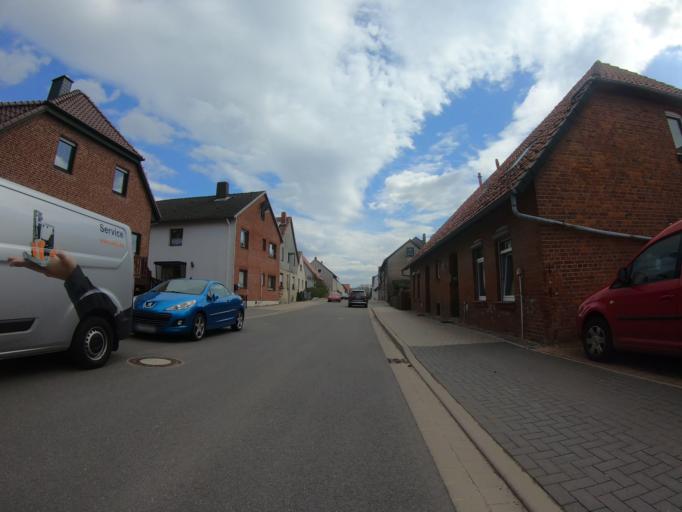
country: DE
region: Lower Saxony
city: Nordstemmen
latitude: 52.1921
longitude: 9.7773
